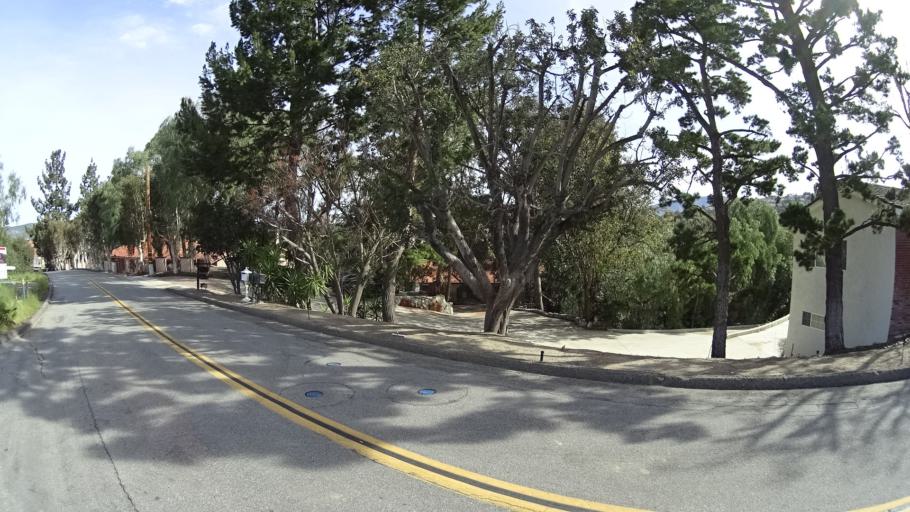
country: US
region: California
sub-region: Orange County
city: Yorba Linda
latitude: 33.8556
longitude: -117.7564
